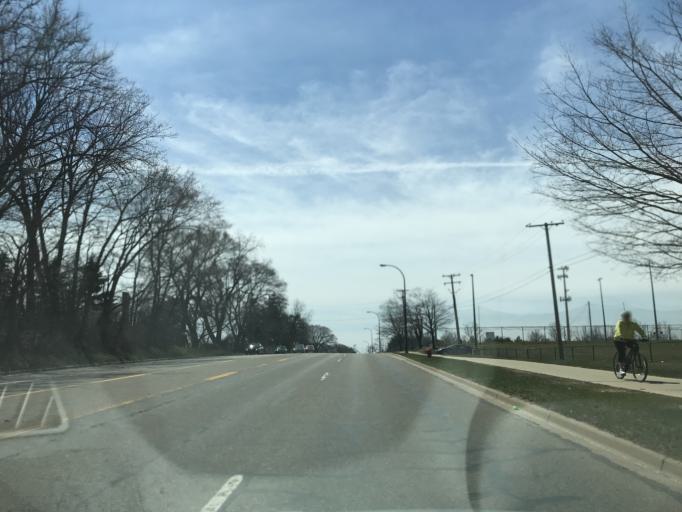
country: US
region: Michigan
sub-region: Washtenaw County
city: Ann Arbor
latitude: 42.2619
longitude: -83.7503
